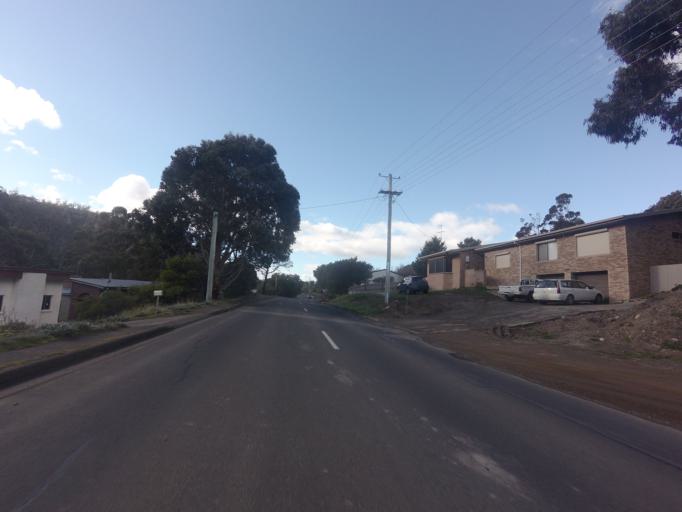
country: AU
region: Tasmania
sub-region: Glenorchy
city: Berriedale
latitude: -42.8177
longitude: 147.2233
